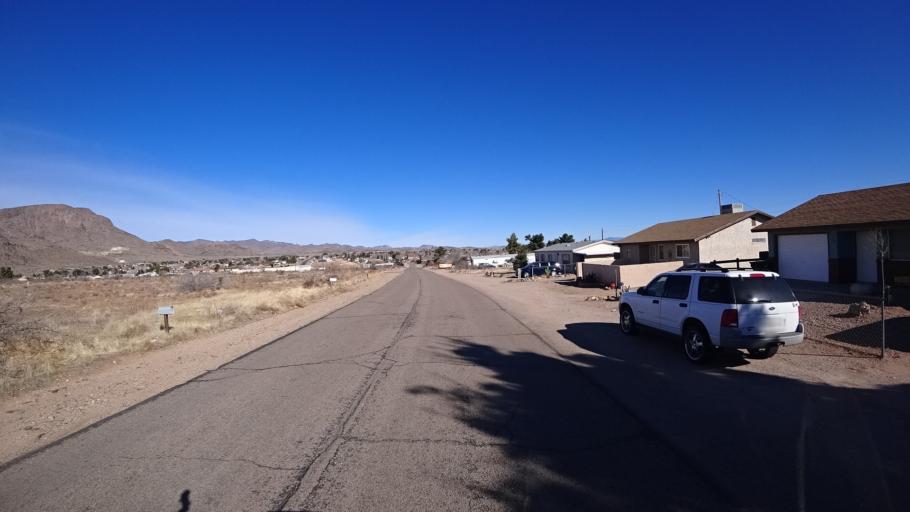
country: US
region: Arizona
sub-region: Mohave County
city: New Kingman-Butler
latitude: 35.2558
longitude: -114.0364
